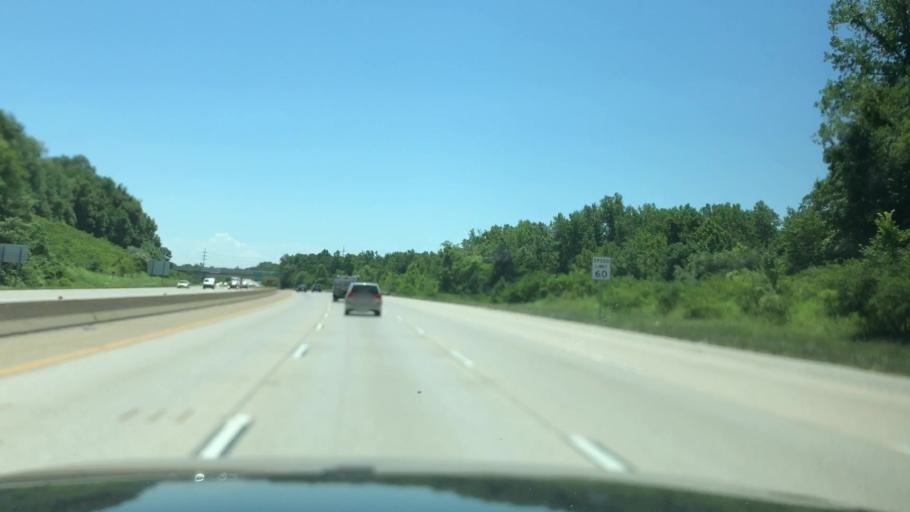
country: US
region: Missouri
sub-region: Saint Louis County
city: Bridgeton
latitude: 38.7793
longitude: -90.4159
